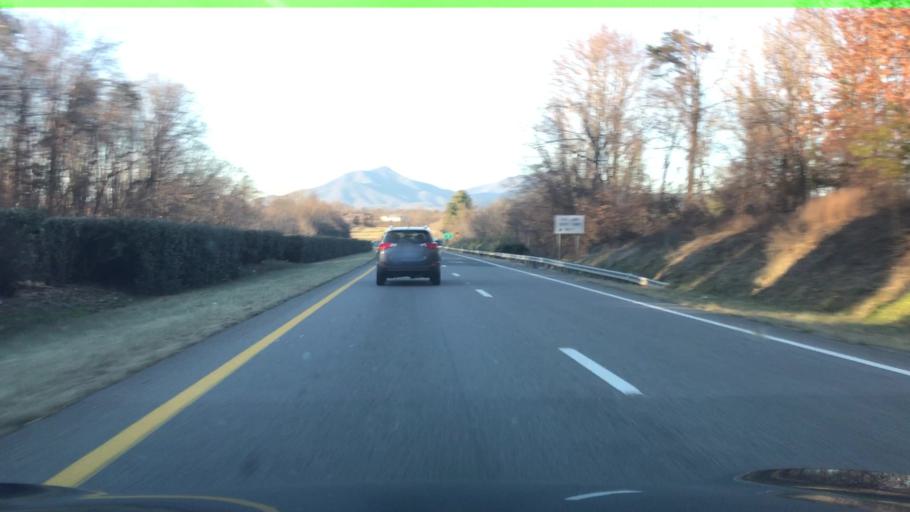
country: US
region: Virginia
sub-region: City of Bedford
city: Bedford
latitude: 37.3304
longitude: -79.5416
